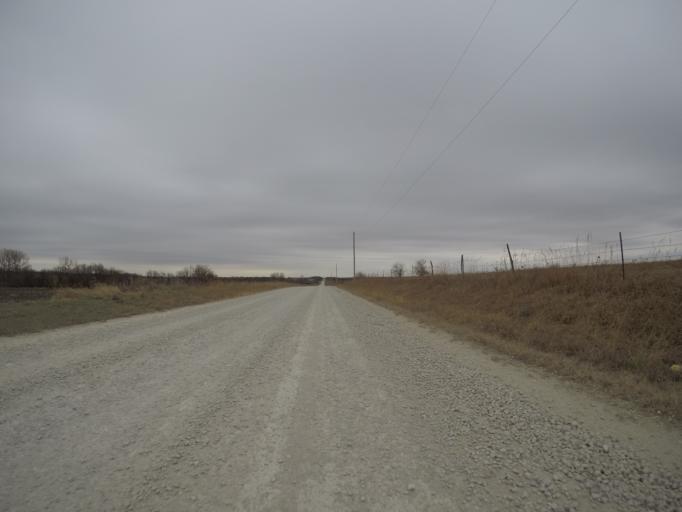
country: US
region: Kansas
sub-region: Wabaunsee County
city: Alma
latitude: 38.8203
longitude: -96.1133
